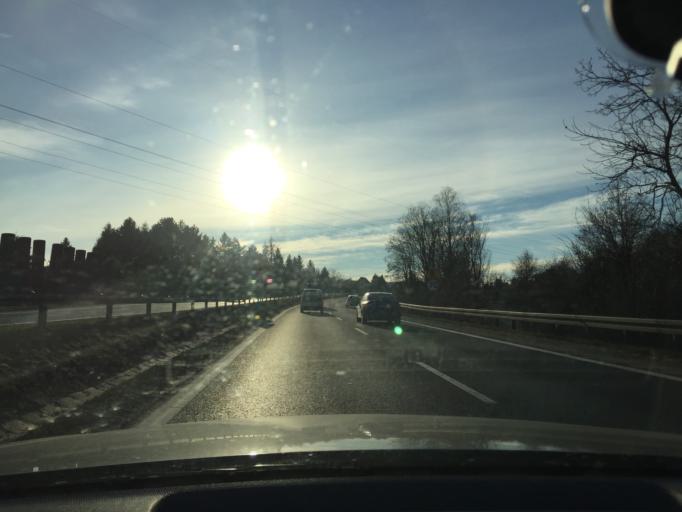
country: PL
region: Lesser Poland Voivodeship
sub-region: Powiat krakowski
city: Libertow
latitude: 49.9652
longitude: 19.8976
